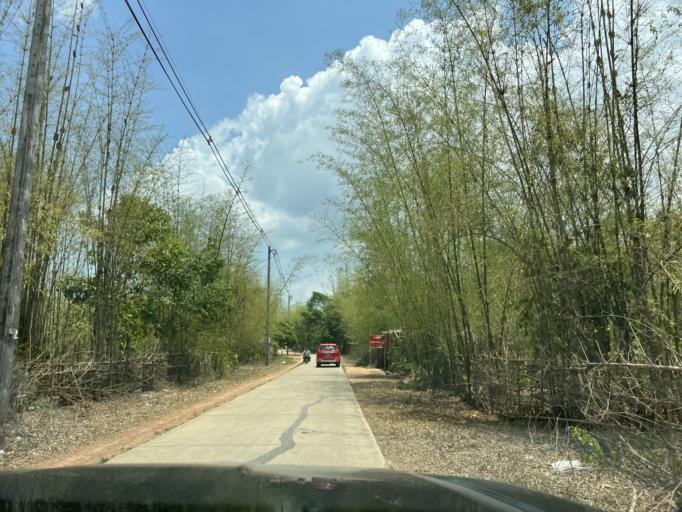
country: MM
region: Ayeyarwady
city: Kyaiklat
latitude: 16.5079
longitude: 95.9019
